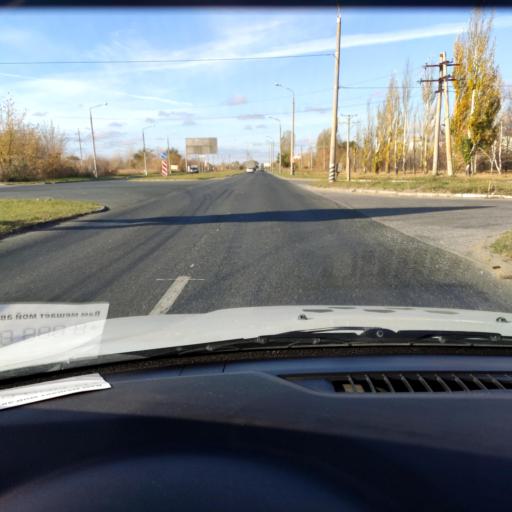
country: RU
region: Samara
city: Tol'yatti
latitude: 53.5577
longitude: 49.3302
